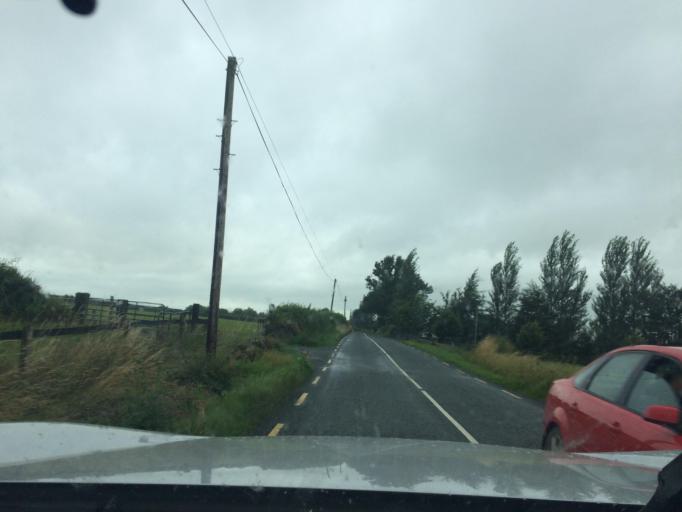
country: IE
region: Munster
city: Cashel
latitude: 52.5375
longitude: -7.8915
